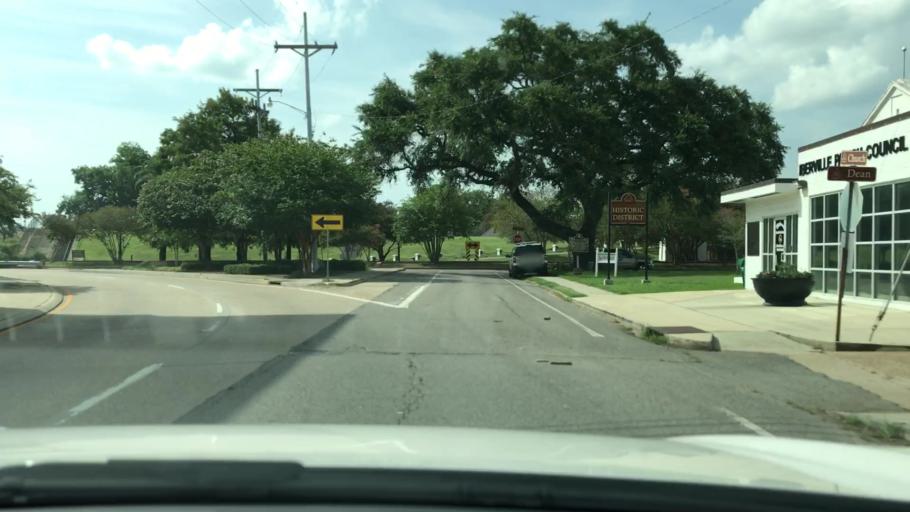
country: US
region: Louisiana
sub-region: Iberville Parish
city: Plaquemine
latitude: 30.2914
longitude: -91.2341
